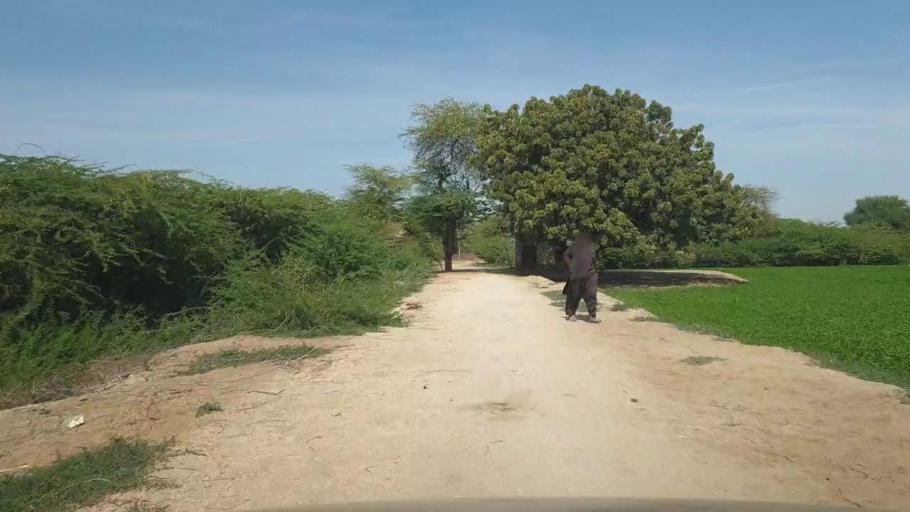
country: PK
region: Sindh
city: Kunri
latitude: 25.3098
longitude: 69.5767
